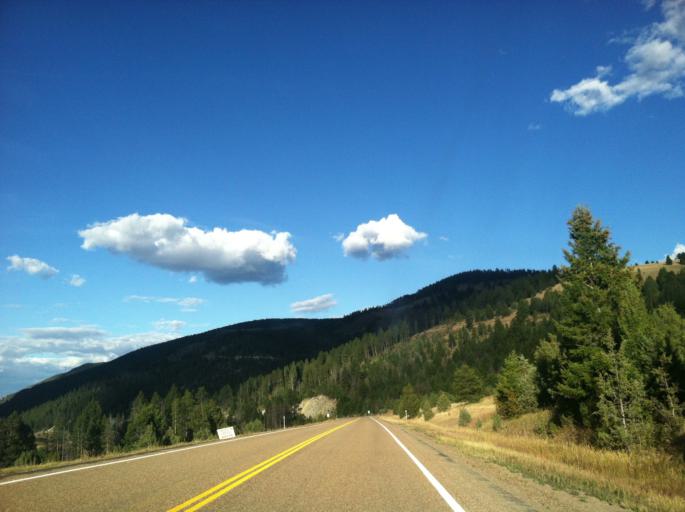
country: US
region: Montana
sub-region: Granite County
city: Philipsburg
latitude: 46.3995
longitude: -113.3029
